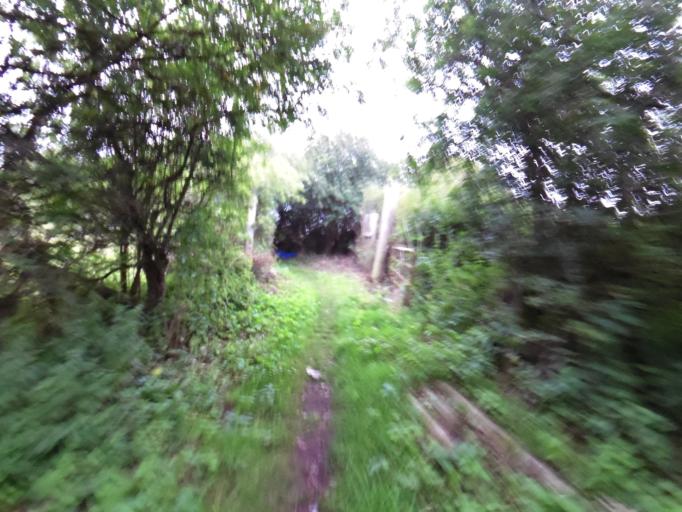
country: GB
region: Scotland
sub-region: Midlothian
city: Dalkeith
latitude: 55.9136
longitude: -3.0867
